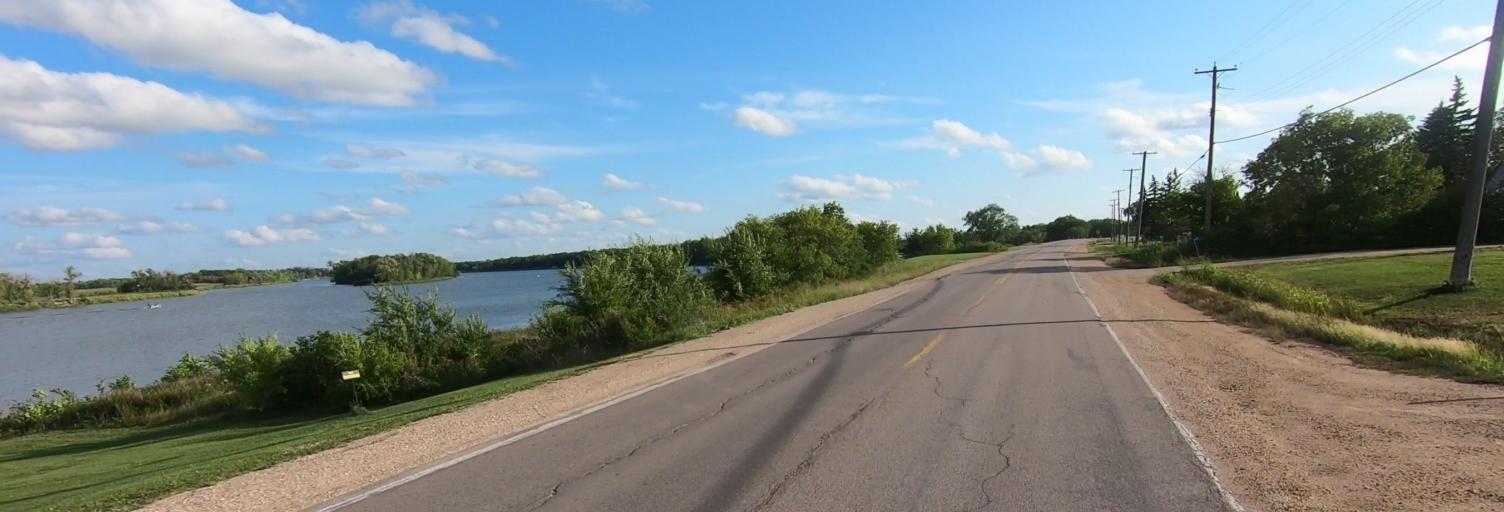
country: CA
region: Manitoba
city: Selkirk
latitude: 50.1717
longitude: -96.8613
